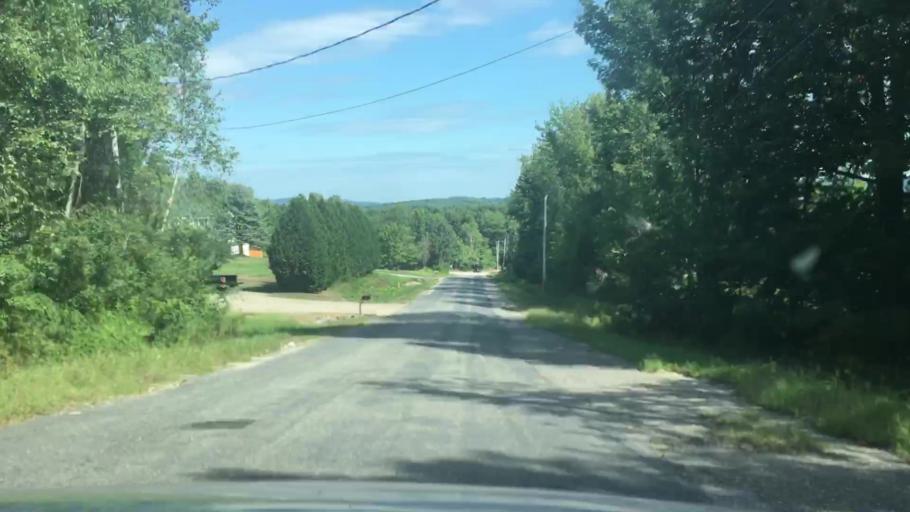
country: US
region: Maine
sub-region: Androscoggin County
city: Turner
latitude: 44.1925
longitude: -70.2592
